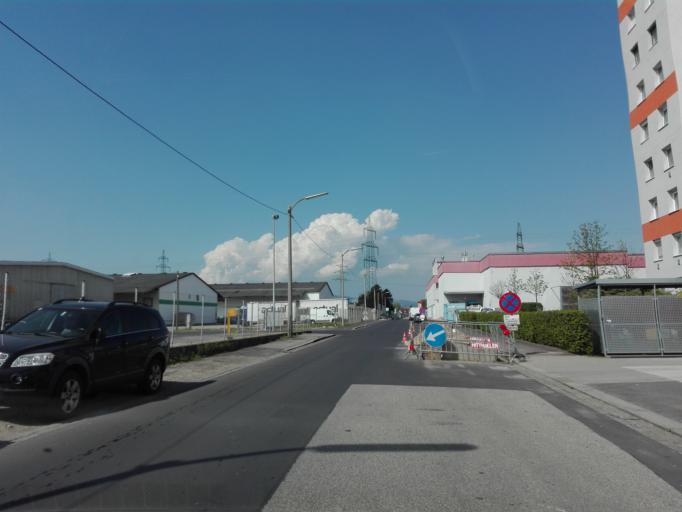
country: AT
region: Upper Austria
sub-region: Politischer Bezirk Linz-Land
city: Ansfelden
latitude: 48.2419
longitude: 14.2763
